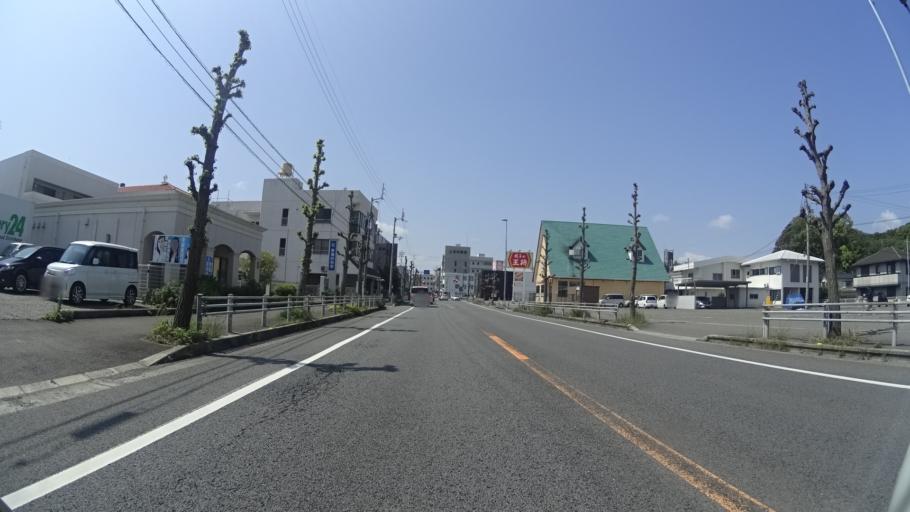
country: JP
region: Tokushima
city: Narutocho-mitsuishi
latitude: 34.1815
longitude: 134.6101
